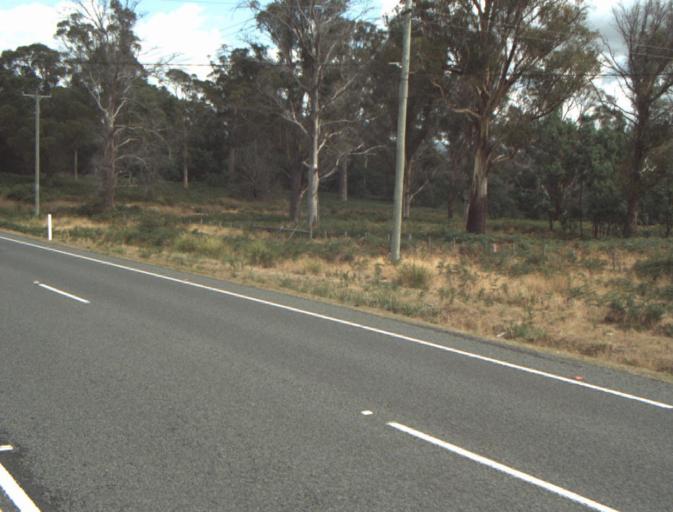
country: AU
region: Tasmania
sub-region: Launceston
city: Mayfield
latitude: -41.2789
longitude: 147.0379
